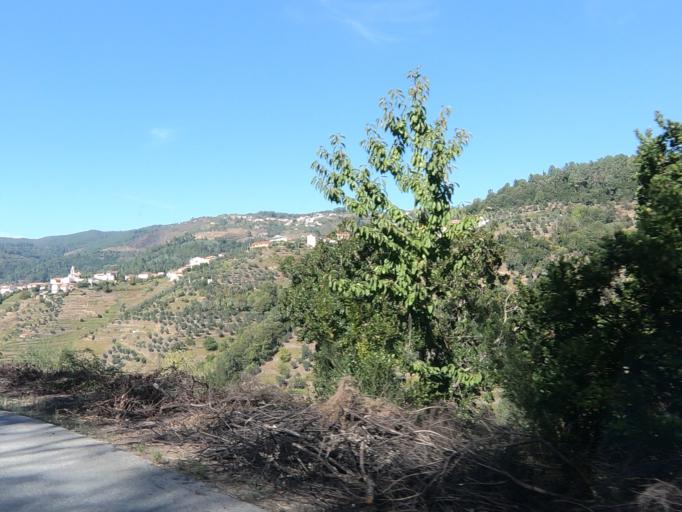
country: PT
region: Vila Real
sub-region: Santa Marta de Penaguiao
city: Santa Marta de Penaguiao
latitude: 41.2404
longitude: -7.8036
